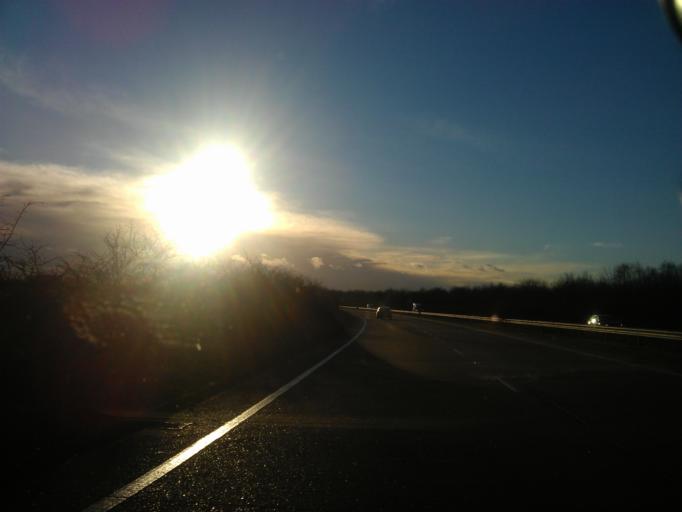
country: GB
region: England
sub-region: Essex
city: Great Bentley
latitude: 51.8755
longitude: 1.0505
